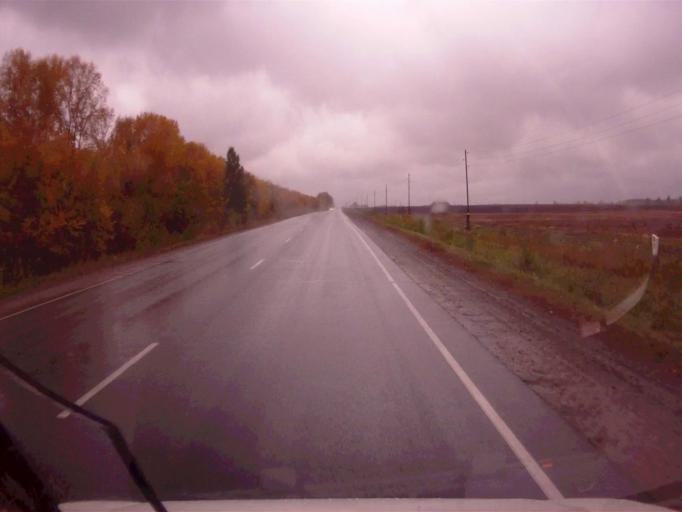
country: RU
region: Chelyabinsk
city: Argayash
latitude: 55.4258
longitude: 61.0030
